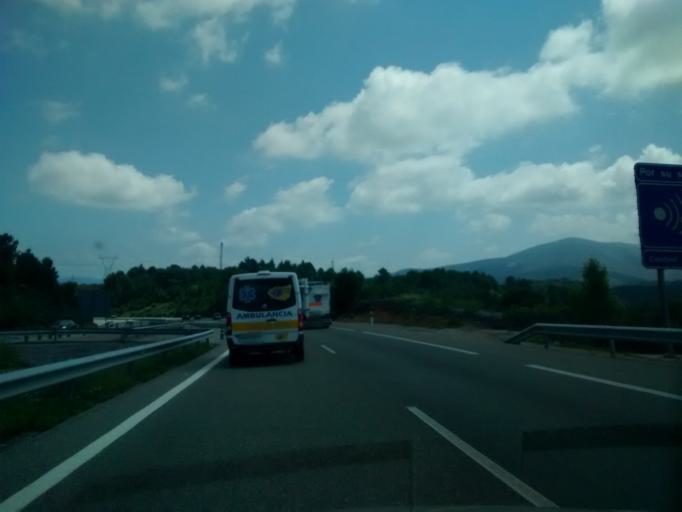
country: ES
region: Castille and Leon
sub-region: Provincia de Leon
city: Molinaseca
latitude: 42.5698
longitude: -6.5414
